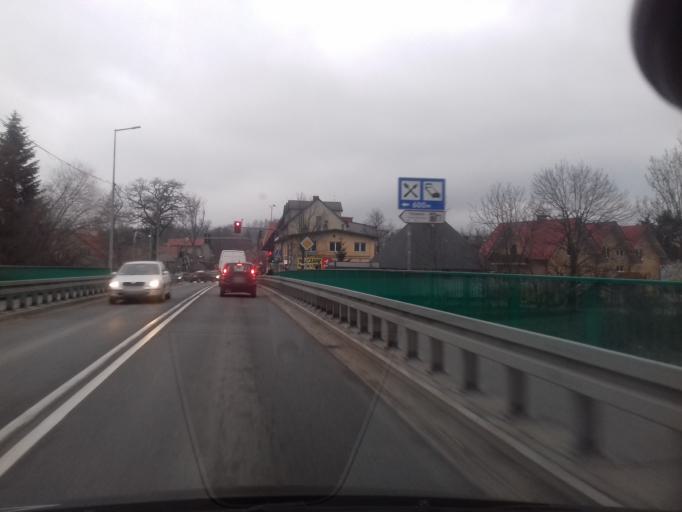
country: PL
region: Lesser Poland Voivodeship
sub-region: Powiat limanowski
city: Mszana Dolna
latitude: 49.6744
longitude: 20.0808
